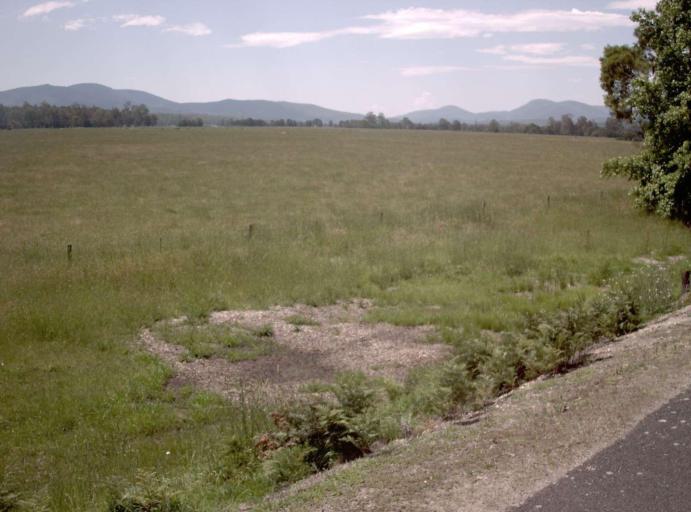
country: AU
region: New South Wales
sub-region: Bombala
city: Bombala
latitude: -37.5691
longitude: 149.1395
